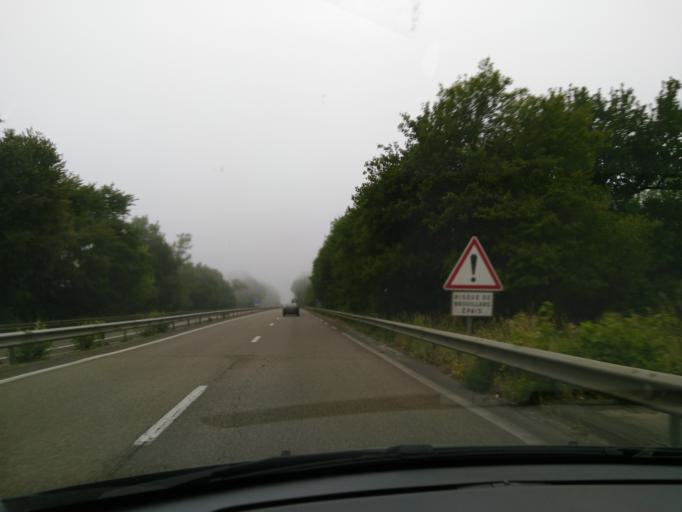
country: FR
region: Aquitaine
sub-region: Departement des Landes
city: Tartas
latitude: 43.8245
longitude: -0.8221
